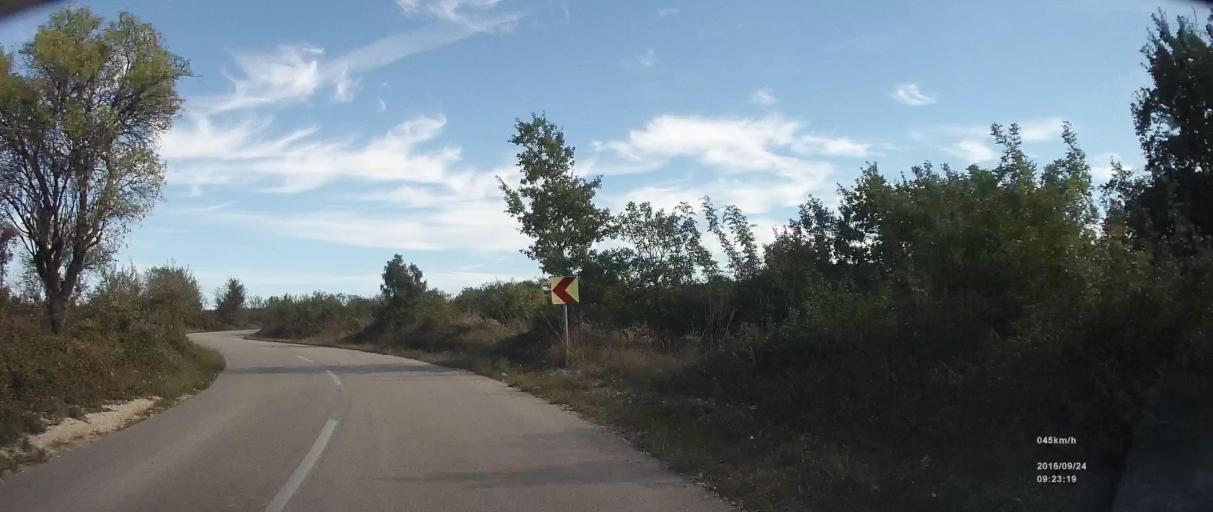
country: HR
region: Zadarska
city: Polaca
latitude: 44.0734
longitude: 15.4752
